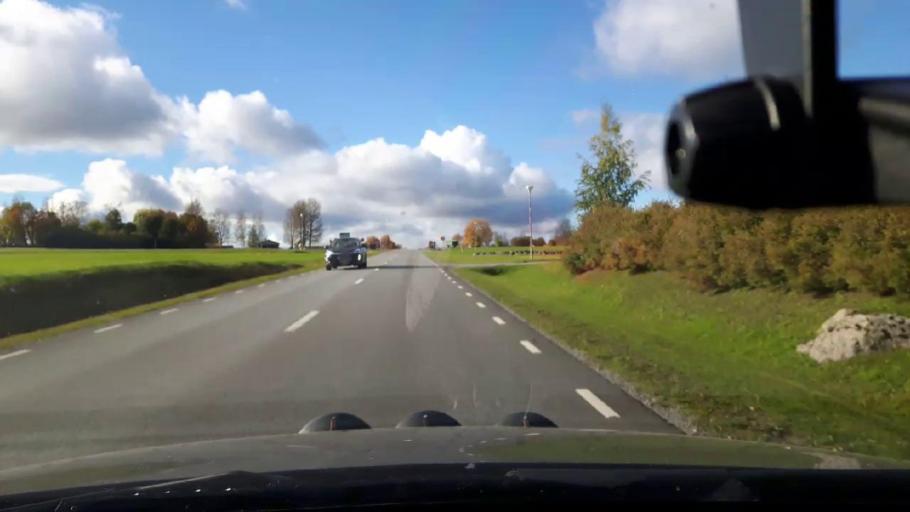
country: SE
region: Jaemtland
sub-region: Bergs Kommun
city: Hoverberg
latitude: 62.9959
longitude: 14.3992
